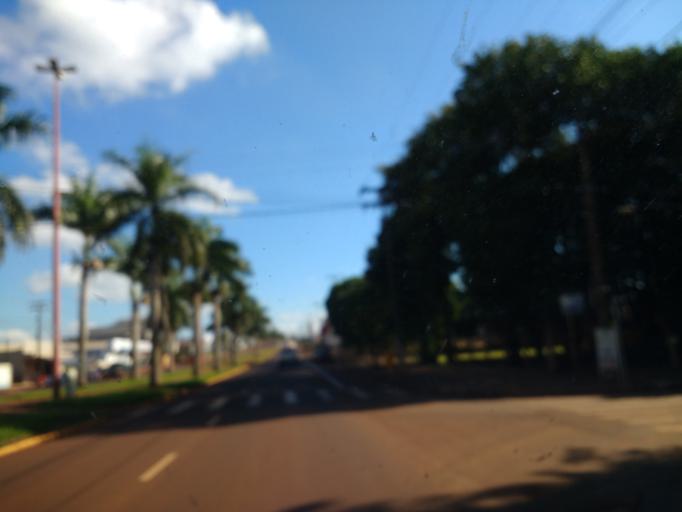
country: BR
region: Parana
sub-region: Palotina
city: Palotina
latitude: -24.4126
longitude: -53.5243
